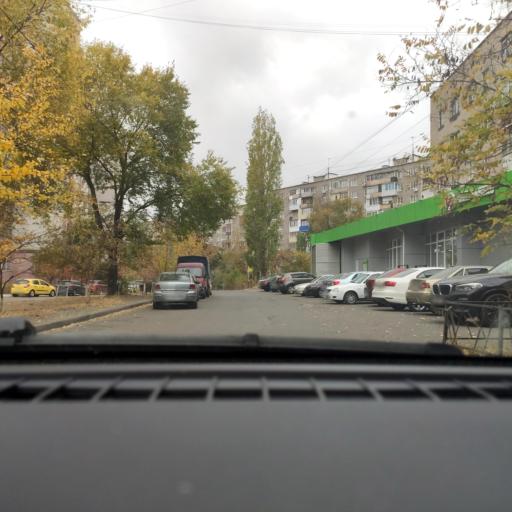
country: RU
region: Voronezj
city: Voronezh
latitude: 51.7177
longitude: 39.2682
